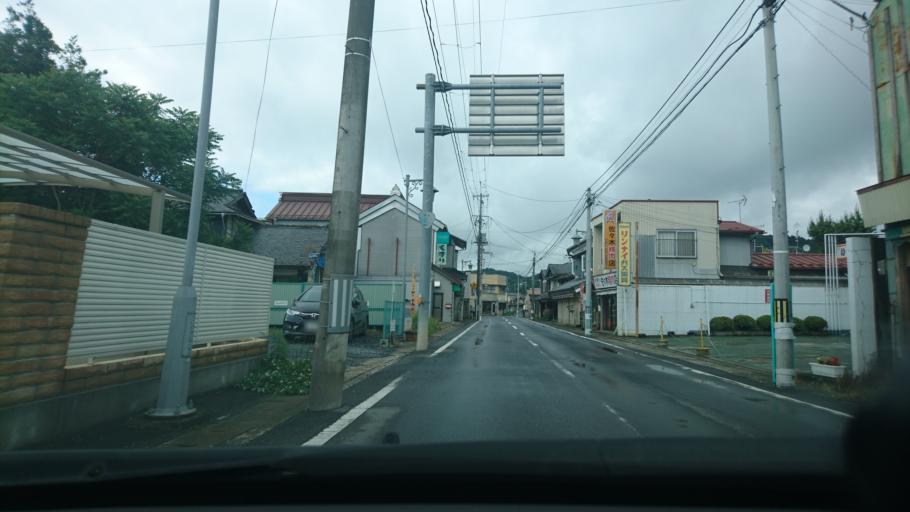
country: JP
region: Miyagi
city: Wakuya
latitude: 38.6541
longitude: 141.2834
